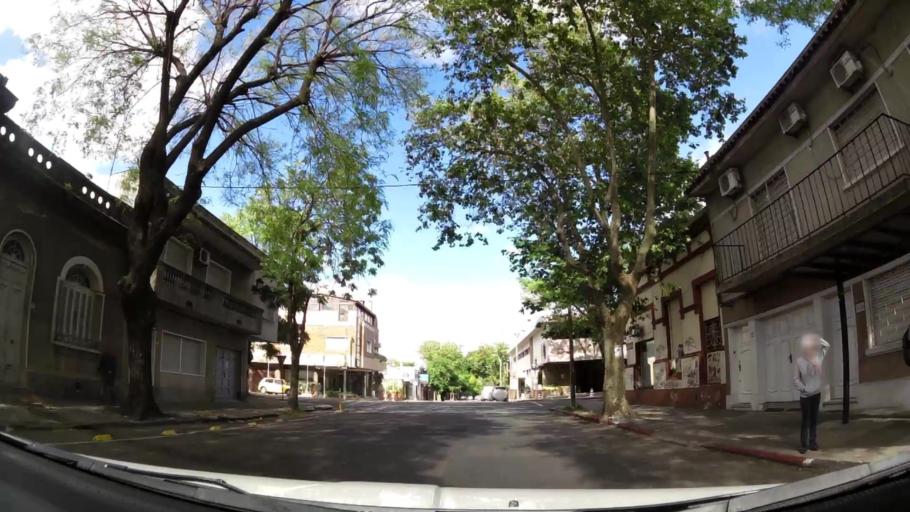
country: UY
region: Montevideo
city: Montevideo
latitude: -34.8884
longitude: -56.1692
